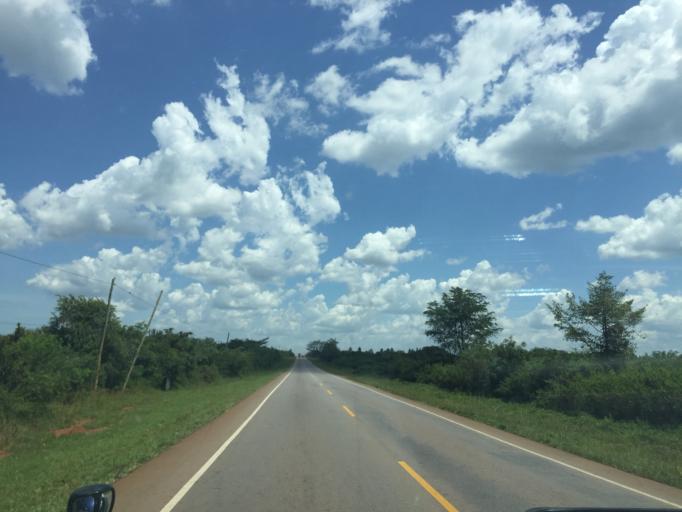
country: UG
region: Central Region
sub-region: Nakasongola District
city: Nakasongola
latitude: 1.3658
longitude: 32.3605
